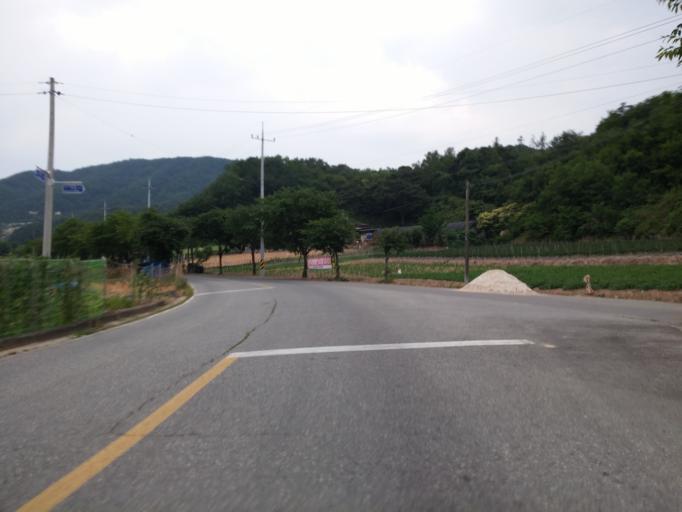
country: KR
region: Chungcheongbuk-do
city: Okcheon
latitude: 36.1943
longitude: 127.5526
